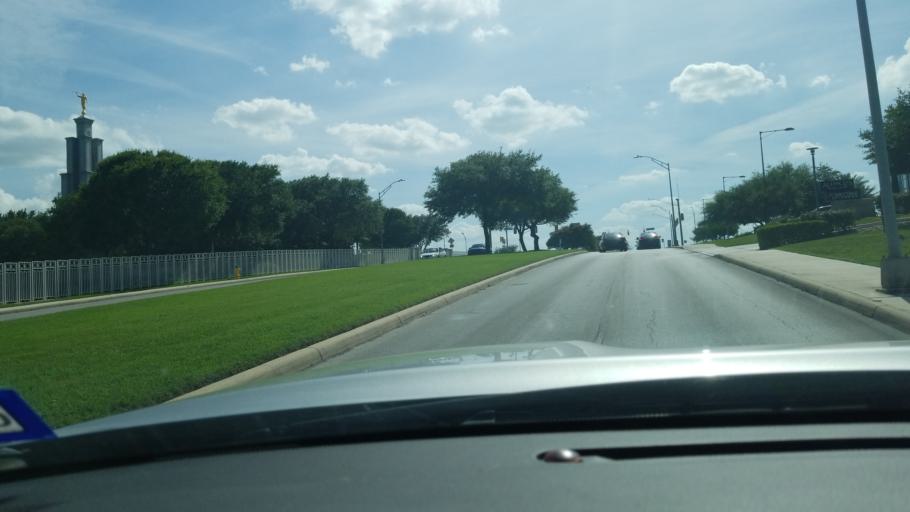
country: US
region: Texas
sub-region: Bexar County
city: Hollywood Park
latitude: 29.6424
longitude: -98.4879
